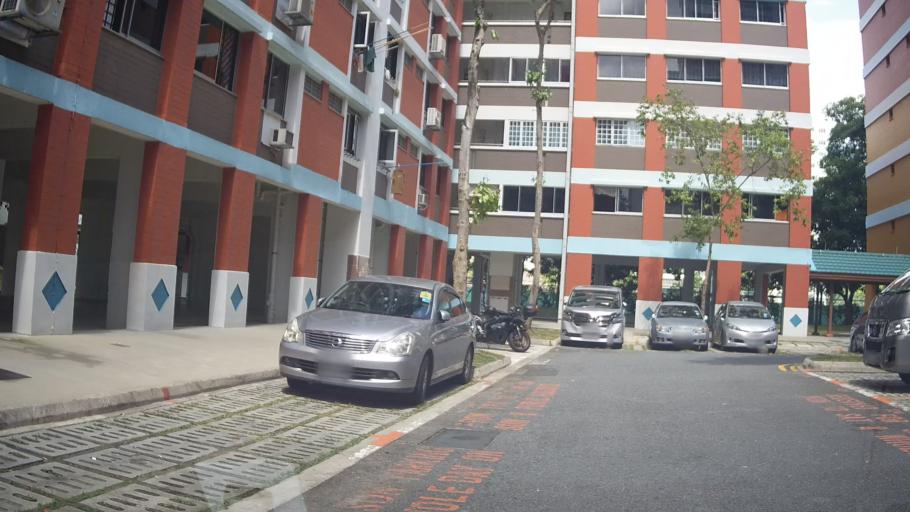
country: SG
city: Singapore
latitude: 1.3505
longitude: 103.9311
